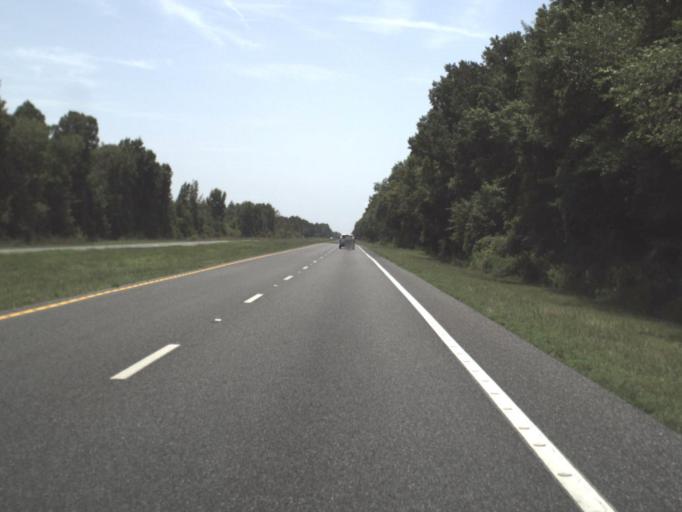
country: US
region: Florida
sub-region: Taylor County
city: Perry
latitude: 29.9299
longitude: -83.4437
